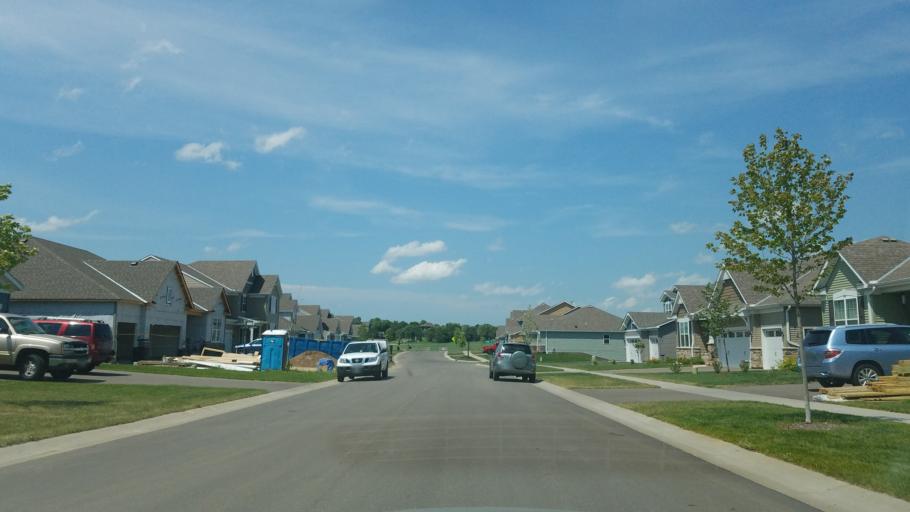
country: US
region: Minnesota
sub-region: Washington County
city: Woodbury
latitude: 44.8853
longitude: -92.9230
